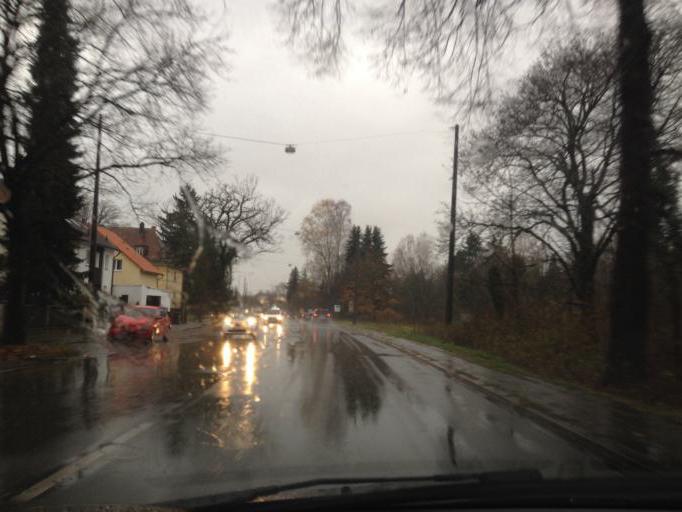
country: DE
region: Bavaria
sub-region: Regierungsbezirk Mittelfranken
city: Schwaig
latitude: 49.4690
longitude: 11.1647
